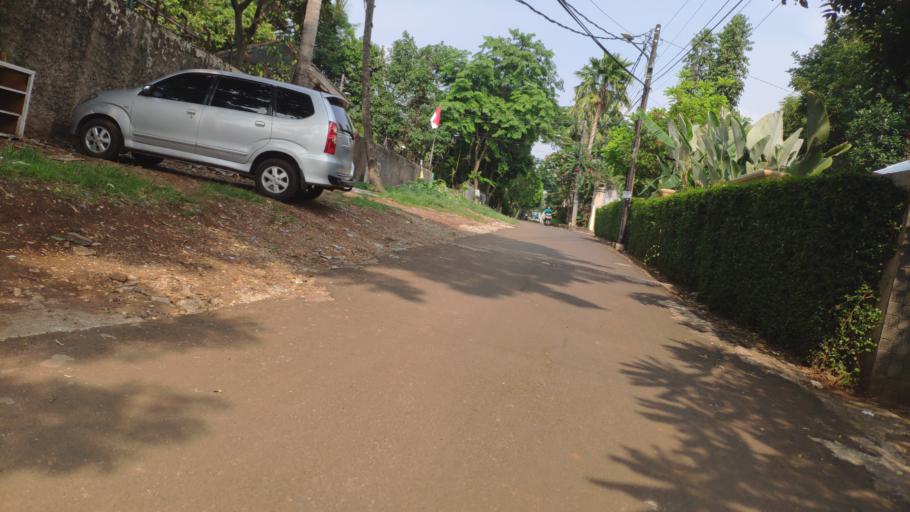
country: ID
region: West Java
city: Depok
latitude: -6.3239
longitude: 106.8136
